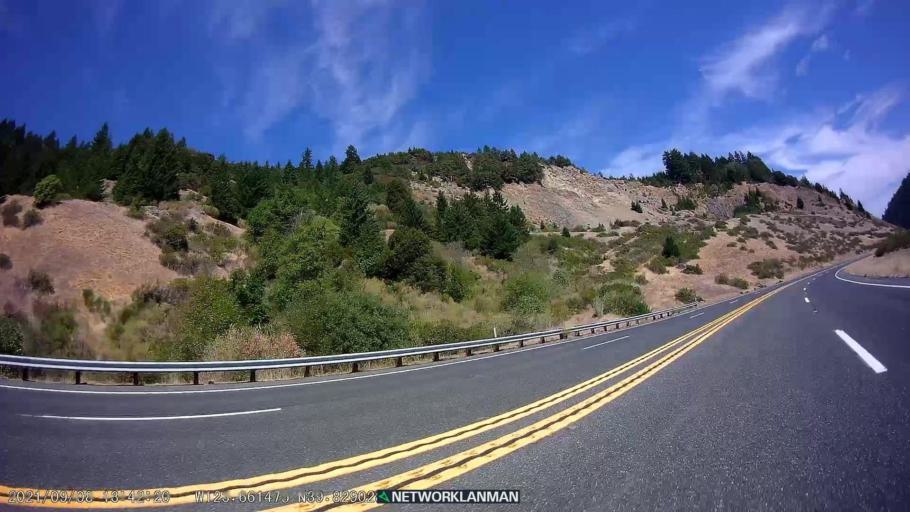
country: US
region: California
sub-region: Mendocino County
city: Laytonville
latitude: 39.8276
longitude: -123.6635
